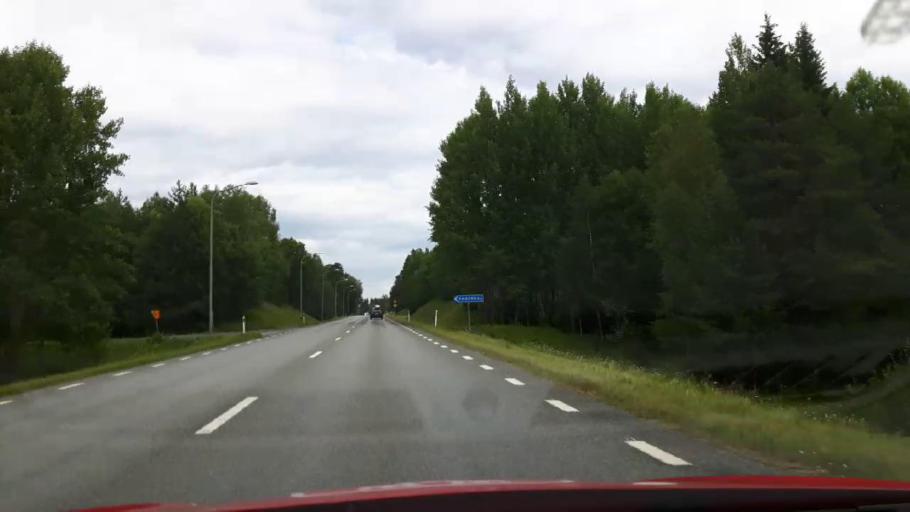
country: SE
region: Jaemtland
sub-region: Stroemsunds Kommun
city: Stroemsund
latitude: 63.6597
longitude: 15.3873
